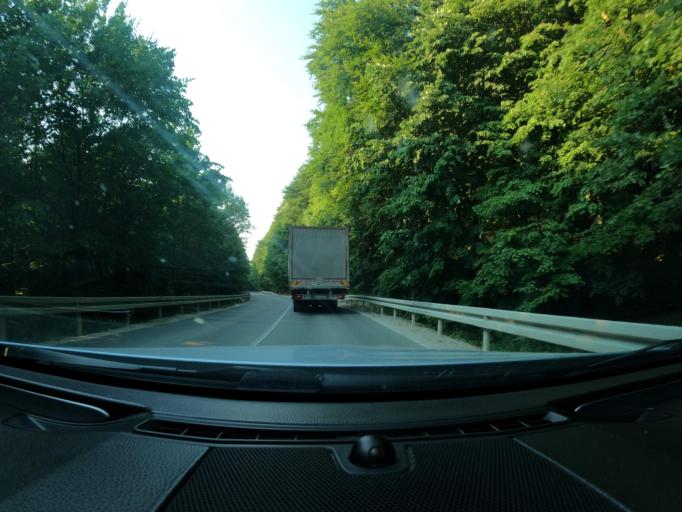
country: RS
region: Autonomna Pokrajina Vojvodina
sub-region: Juznobacki Okrug
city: Beocin
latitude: 45.1596
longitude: 19.7143
